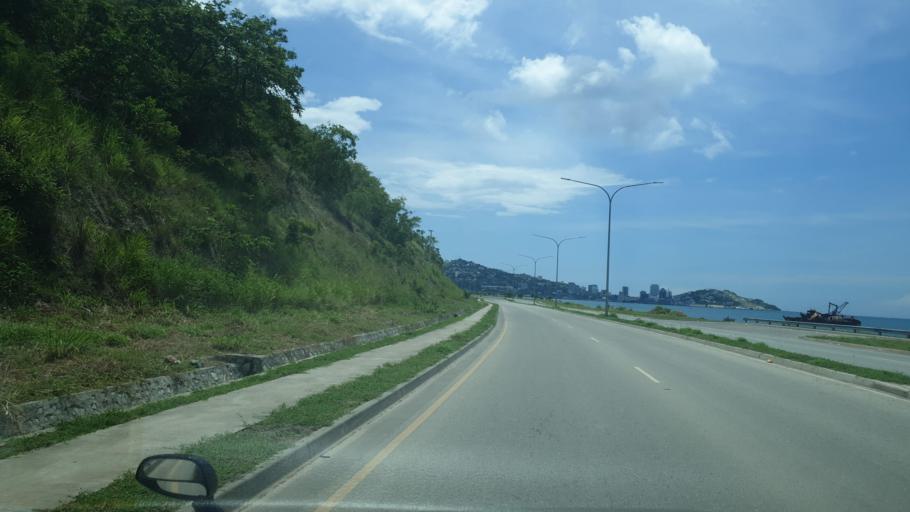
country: PG
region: National Capital
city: Port Moresby
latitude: -9.4436
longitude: 147.1407
